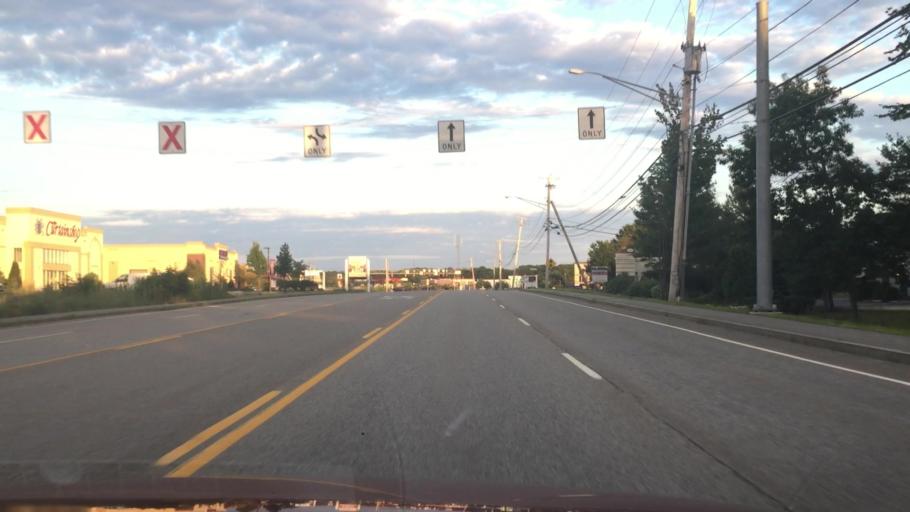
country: US
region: Maine
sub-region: Cumberland County
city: South Portland Gardens
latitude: 43.6367
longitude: -70.3222
